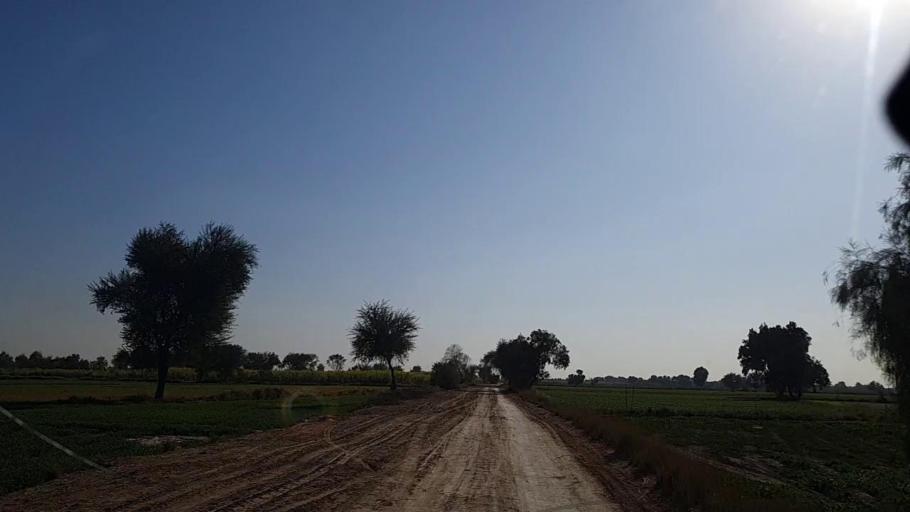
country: PK
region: Sindh
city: Khanpur
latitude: 27.7789
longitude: 69.3662
